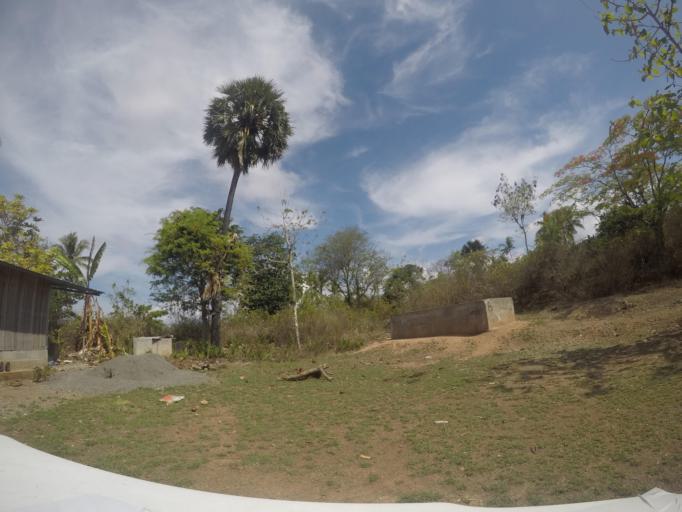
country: TL
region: Baucau
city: Baucau
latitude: -8.4669
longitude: 126.4629
